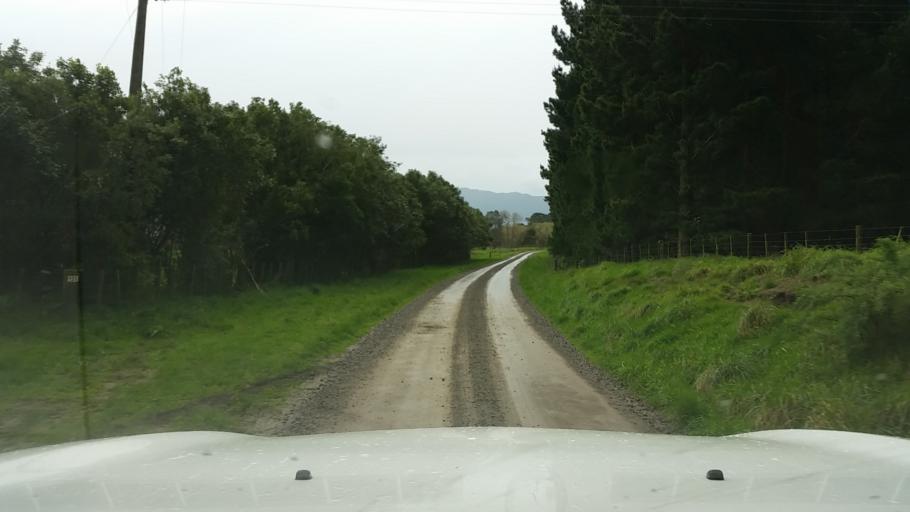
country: NZ
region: Wellington
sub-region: Upper Hutt City
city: Upper Hutt
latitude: -41.2977
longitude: 175.2022
